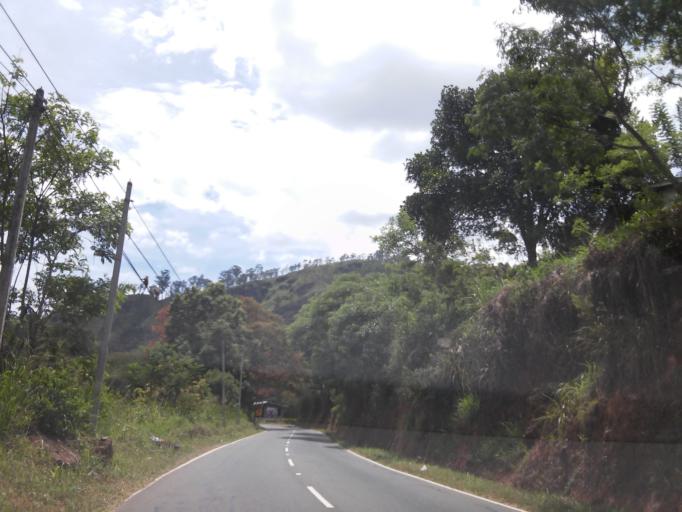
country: LK
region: Uva
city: Haputale
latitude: 6.8690
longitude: 80.9523
